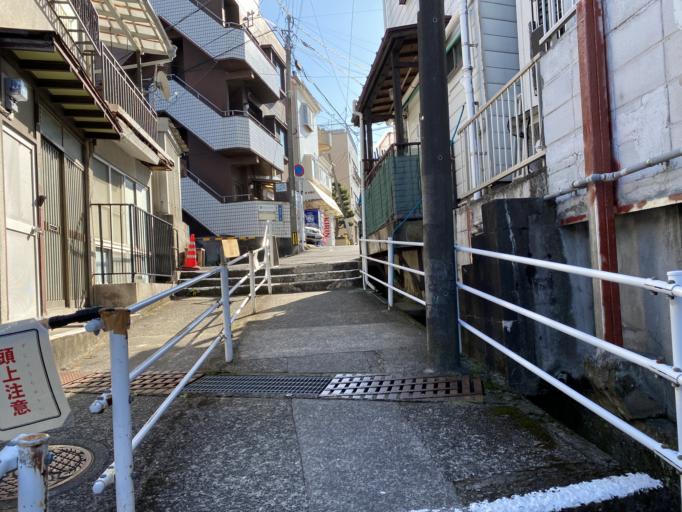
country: JP
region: Nagasaki
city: Nagasaki-shi
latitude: 32.7569
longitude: 129.8613
